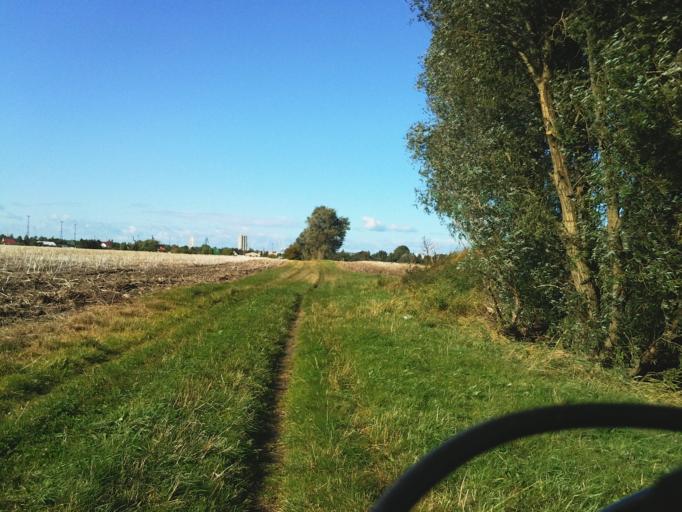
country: DE
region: Mecklenburg-Vorpommern
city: Dierkow-West
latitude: 54.1277
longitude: 12.1155
